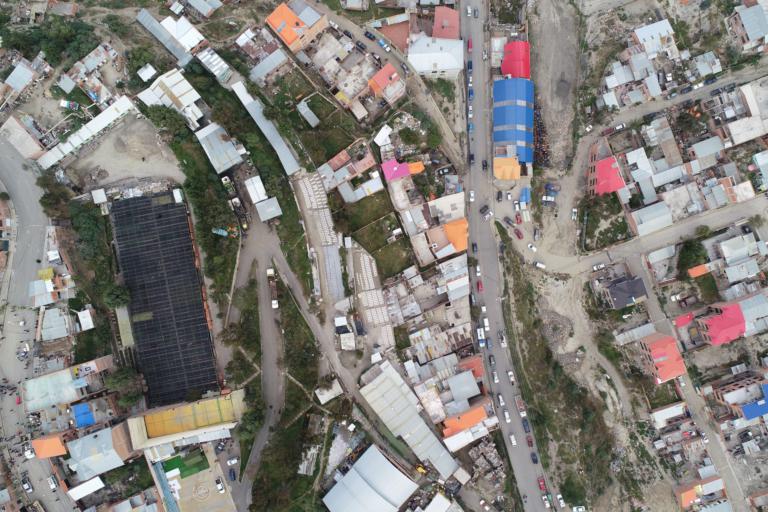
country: BO
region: La Paz
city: La Paz
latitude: -16.5209
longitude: -68.1244
